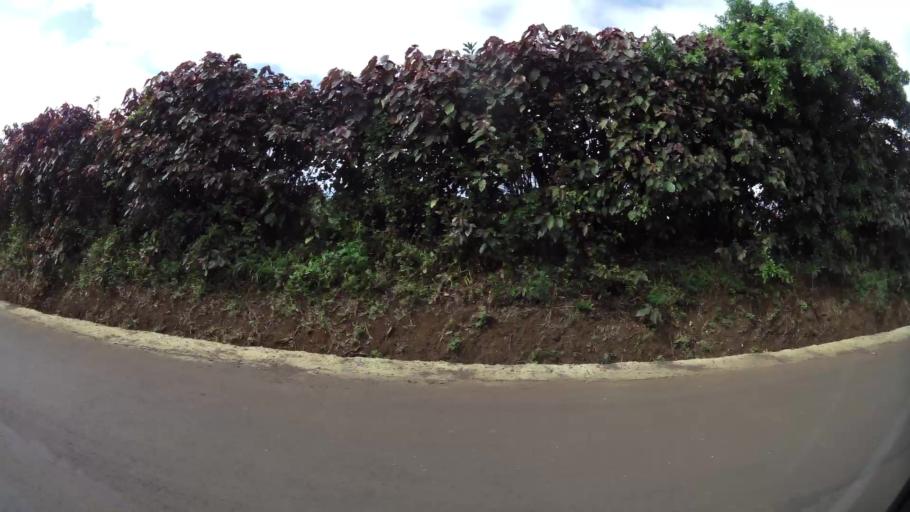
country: RE
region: Reunion
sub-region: Reunion
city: Sainte-Marie
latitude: -20.9021
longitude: 55.5698
